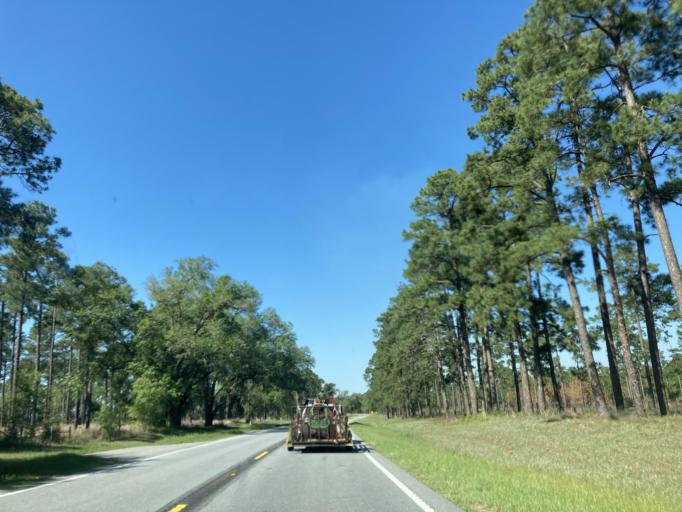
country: US
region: Georgia
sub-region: Baker County
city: Newton
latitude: 31.3902
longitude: -84.2798
